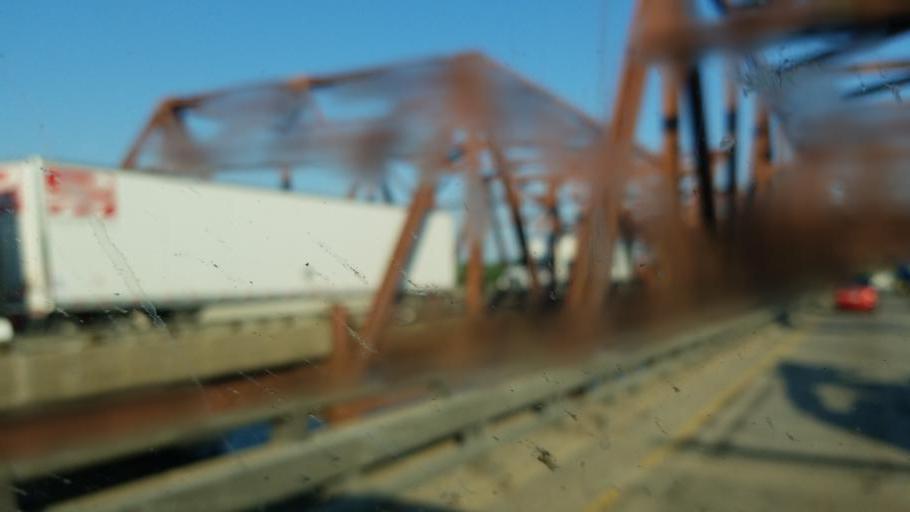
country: US
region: Illinois
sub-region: Will County
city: Joliet
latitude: 41.5113
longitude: -88.0902
